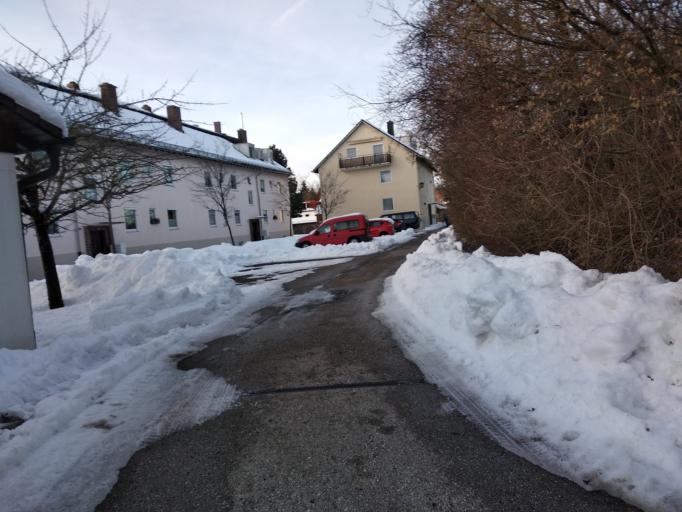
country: DE
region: Bavaria
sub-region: Upper Bavaria
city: Kirchseeon
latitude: 48.0744
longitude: 11.8799
